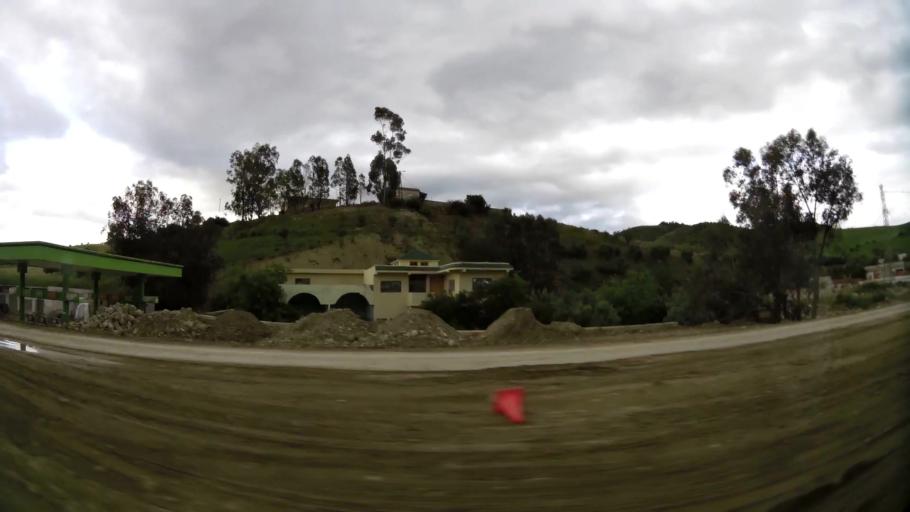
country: MA
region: Taza-Al Hoceima-Taounate
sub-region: Taza
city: Taza
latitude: 34.3517
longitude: -3.9212
